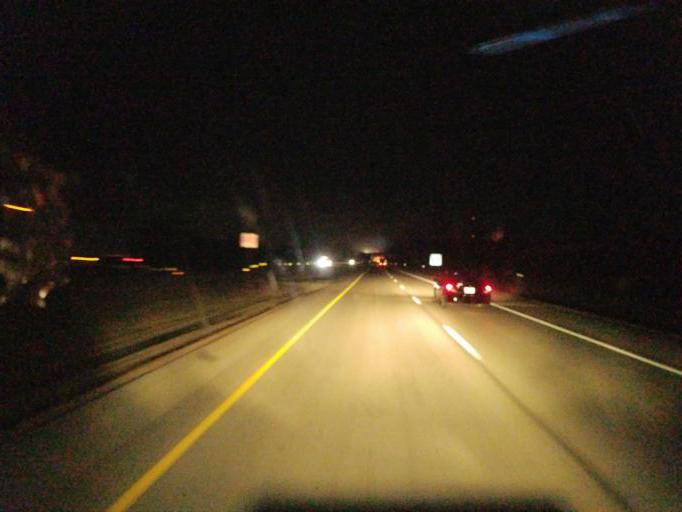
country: US
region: Iowa
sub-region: Madison County
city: Earlham
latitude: 41.5177
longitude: -94.1498
